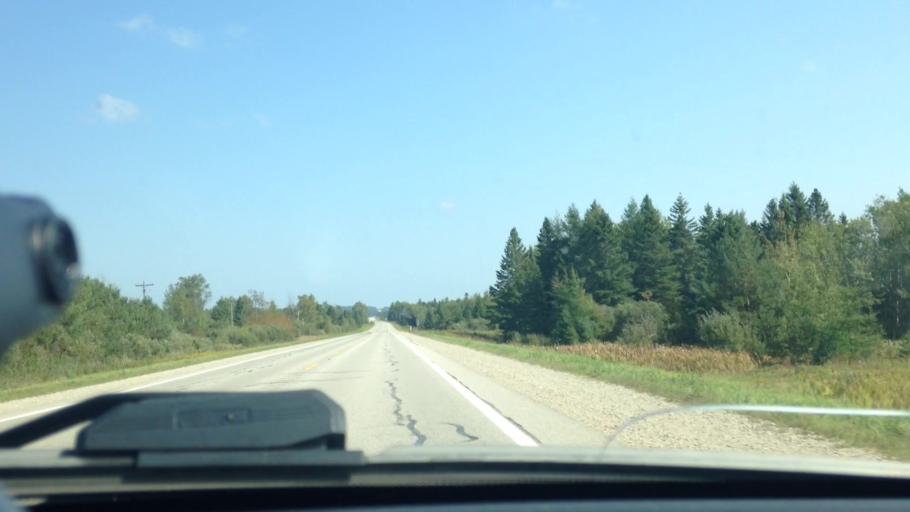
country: US
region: Michigan
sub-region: Luce County
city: Newberry
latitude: 46.3102
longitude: -85.6256
